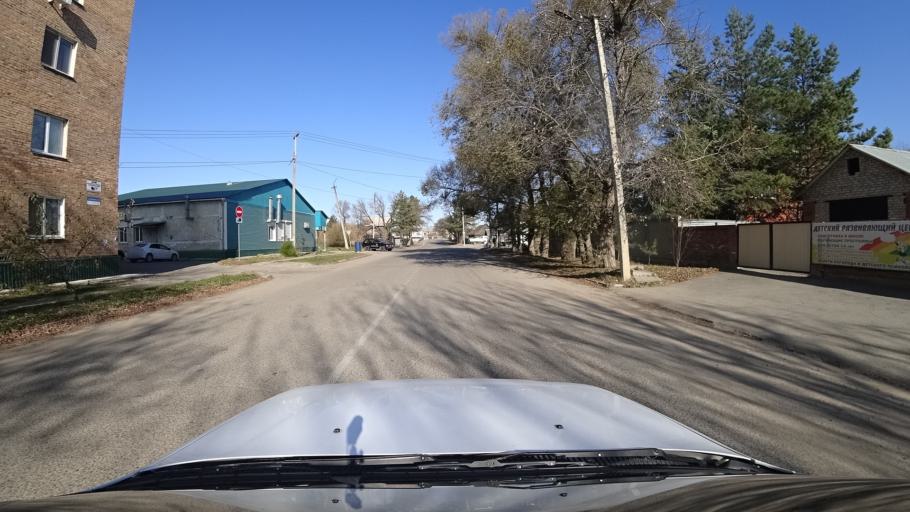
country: RU
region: Primorskiy
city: Dal'nerechensk
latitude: 45.9368
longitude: 133.7327
